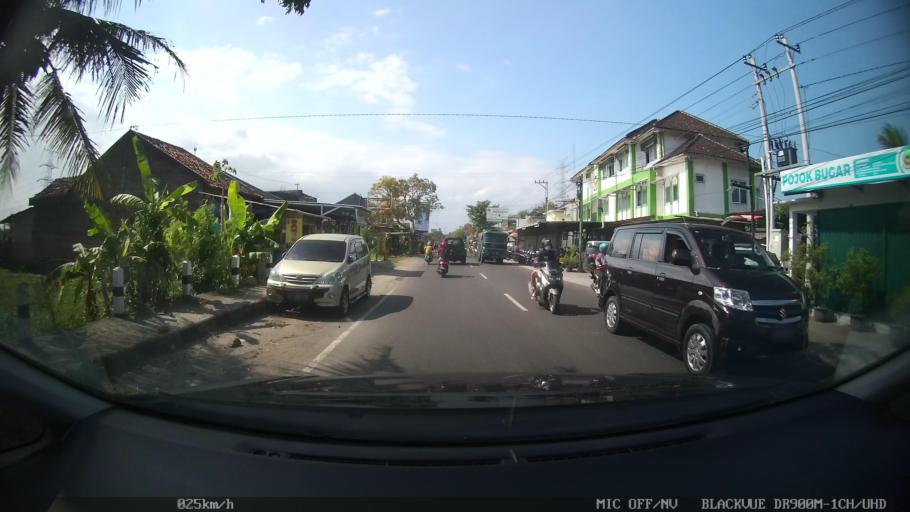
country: ID
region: Daerah Istimewa Yogyakarta
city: Sewon
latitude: -7.8868
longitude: 110.3876
